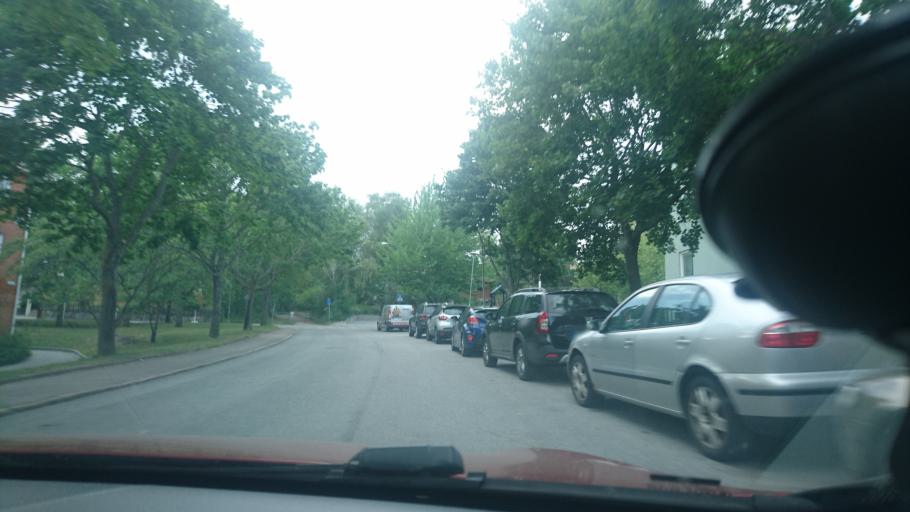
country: SE
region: Stockholm
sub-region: Upplands Vasby Kommun
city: Upplands Vaesby
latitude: 59.5233
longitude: 17.8946
